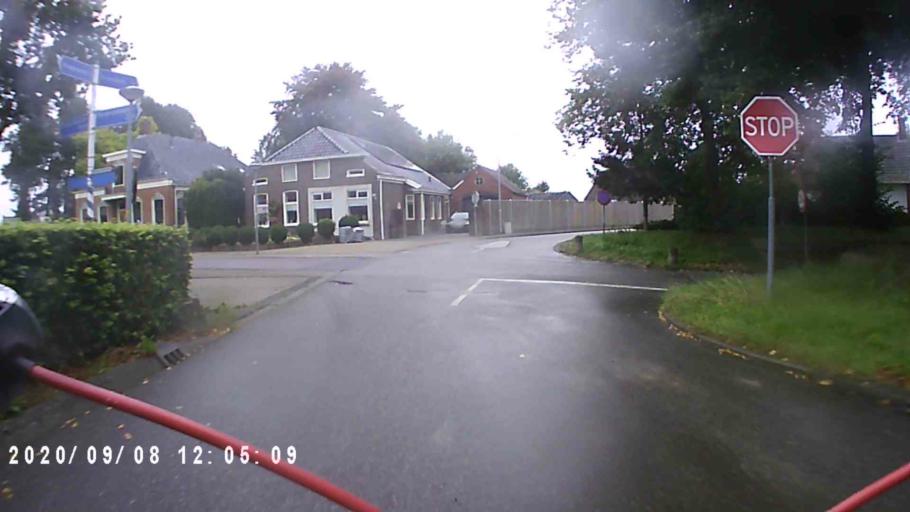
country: NL
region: Groningen
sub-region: Gemeente Veendam
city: Veendam
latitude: 53.1090
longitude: 6.8249
